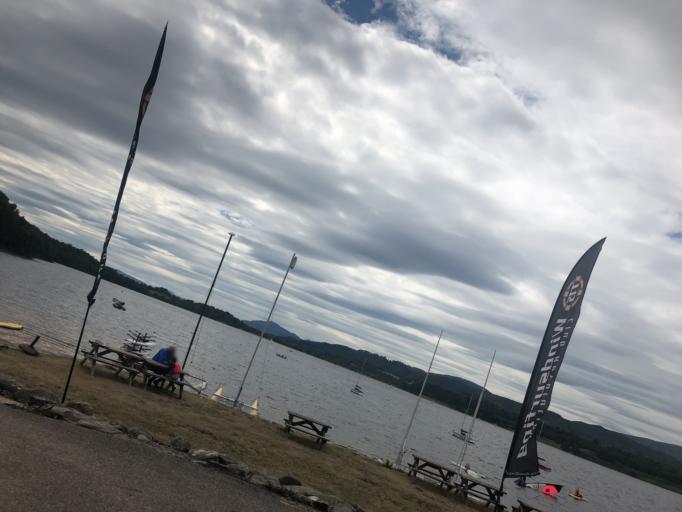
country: GB
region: Scotland
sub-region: Highland
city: Aviemore
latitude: 57.1172
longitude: -3.9208
